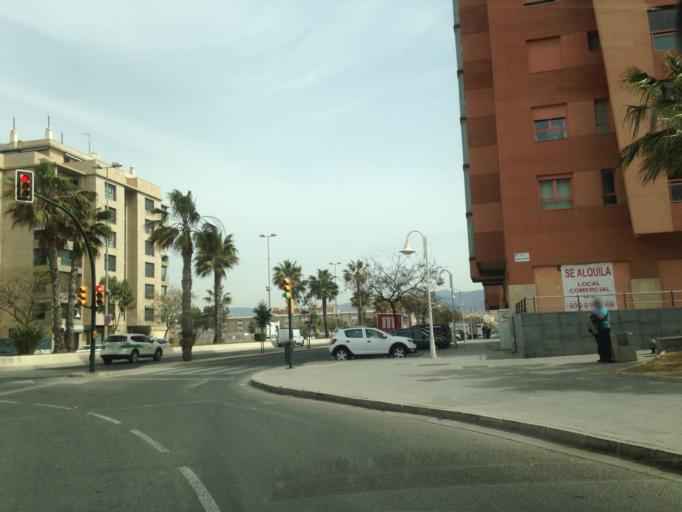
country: ES
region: Andalusia
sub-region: Provincia de Malaga
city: Malaga
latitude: 36.6940
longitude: -4.4403
